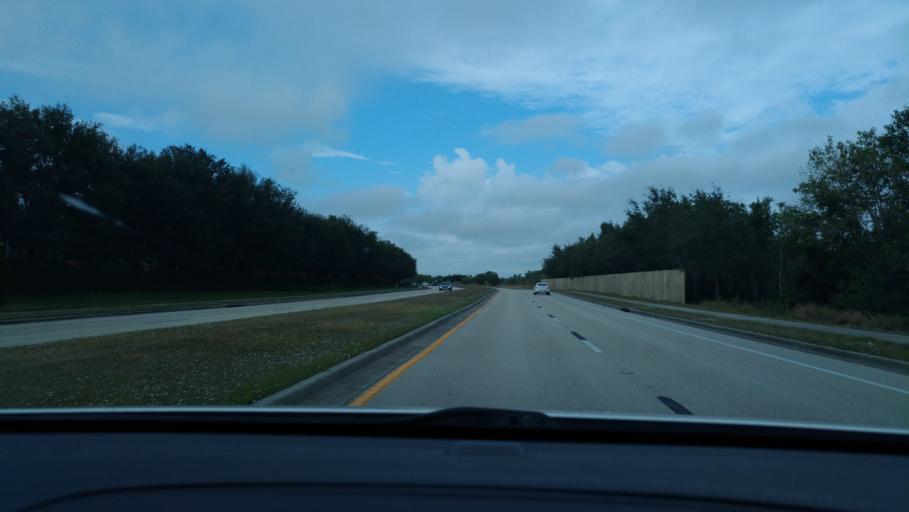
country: US
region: Florida
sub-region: Lee County
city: Estero
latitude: 26.4135
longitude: -81.8047
